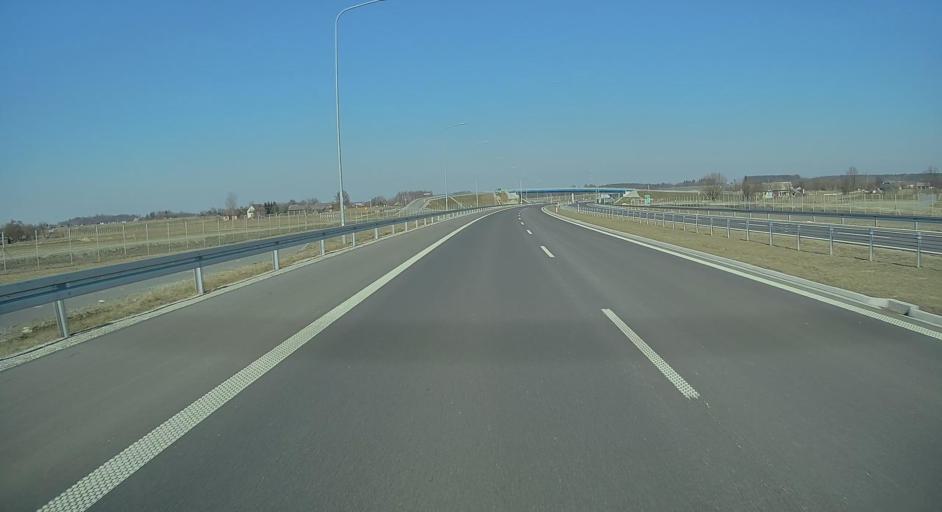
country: PL
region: Lublin Voivodeship
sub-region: Powiat janowski
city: Modliborzyce
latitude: 50.7496
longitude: 22.2937
